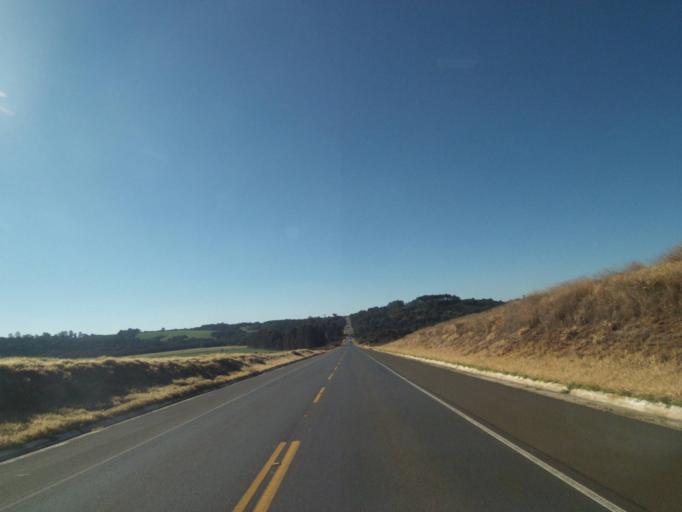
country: BR
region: Parana
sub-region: Tibagi
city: Tibagi
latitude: -24.6163
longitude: -50.4473
